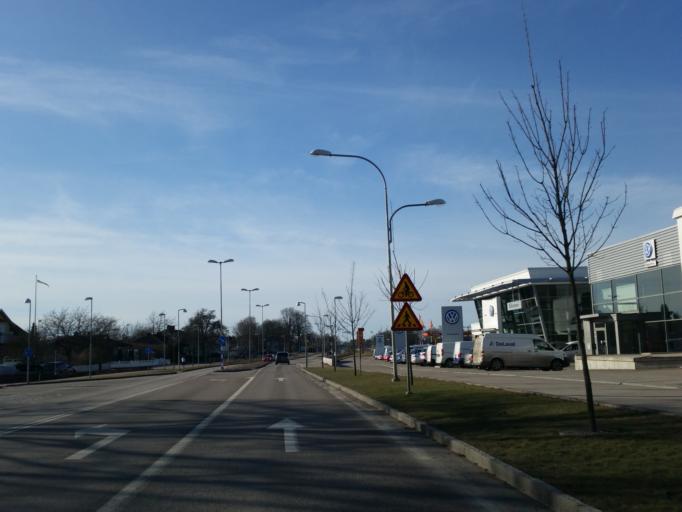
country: SE
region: Kalmar
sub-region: Kalmar Kommun
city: Kalmar
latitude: 56.6656
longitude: 16.3299
